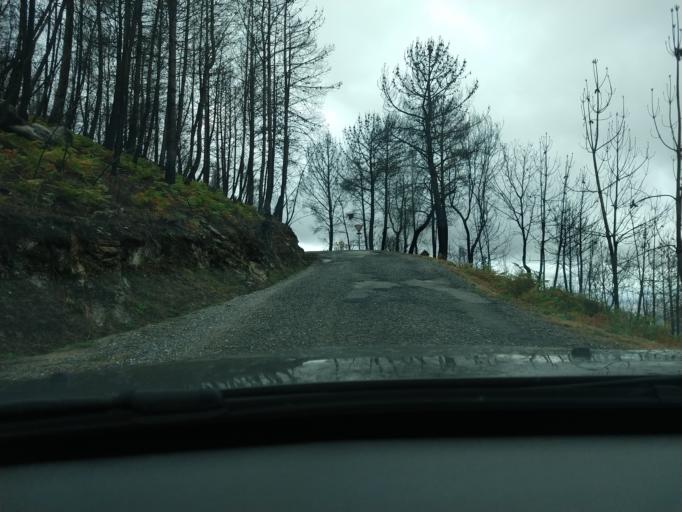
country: PT
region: Guarda
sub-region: Seia
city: Seia
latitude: 40.4197
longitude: -7.6744
